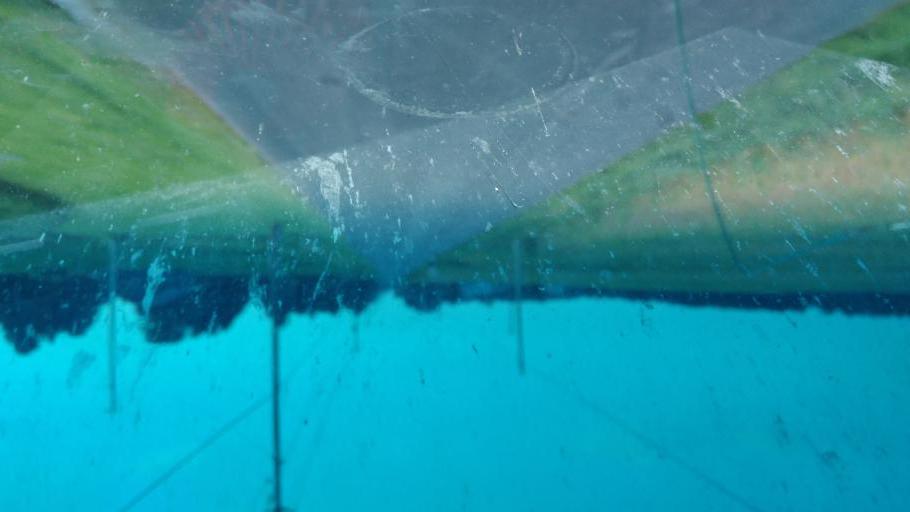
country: US
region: Ohio
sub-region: Crawford County
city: Galion
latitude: 40.7805
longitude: -82.8195
